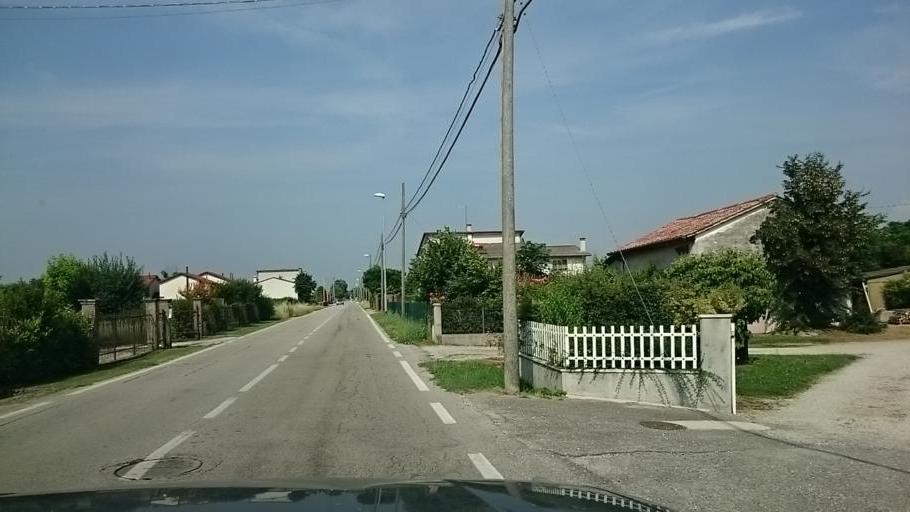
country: IT
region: Veneto
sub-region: Provincia di Treviso
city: Castello di Godego
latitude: 45.6875
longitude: 11.8687
